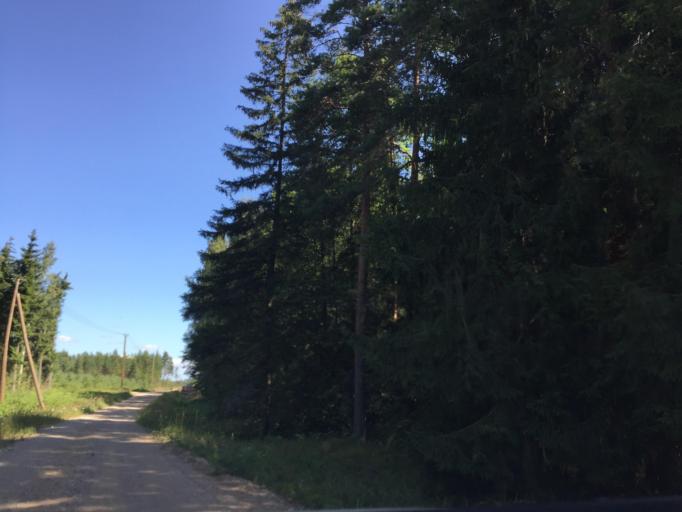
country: LV
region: Talsu Rajons
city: Stende
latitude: 57.1714
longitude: 22.3022
